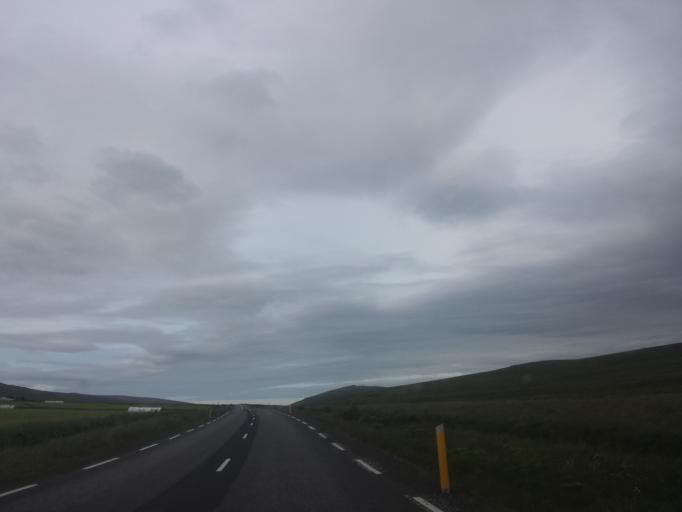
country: IS
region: Northeast
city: Laugar
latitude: 65.7304
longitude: -17.5916
